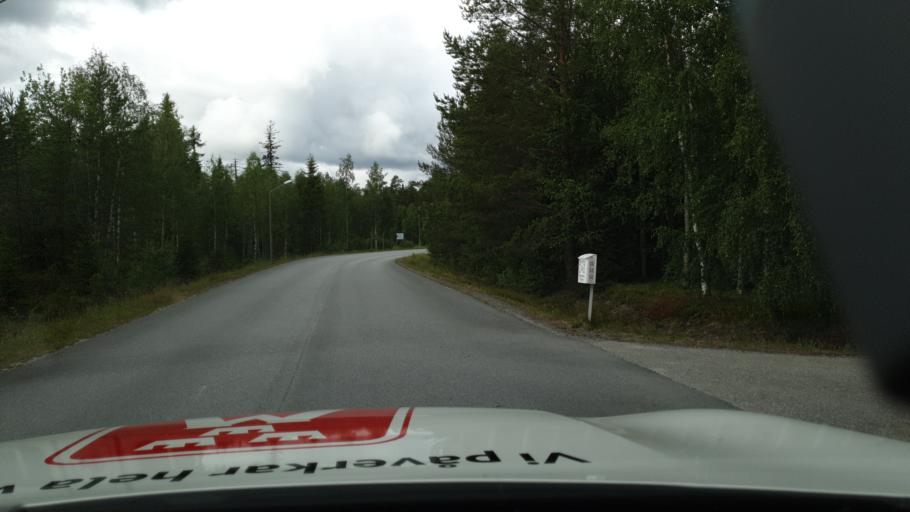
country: SE
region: Vaesterbotten
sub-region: Umea Kommun
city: Hoernefors
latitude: 63.6395
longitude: 19.9267
